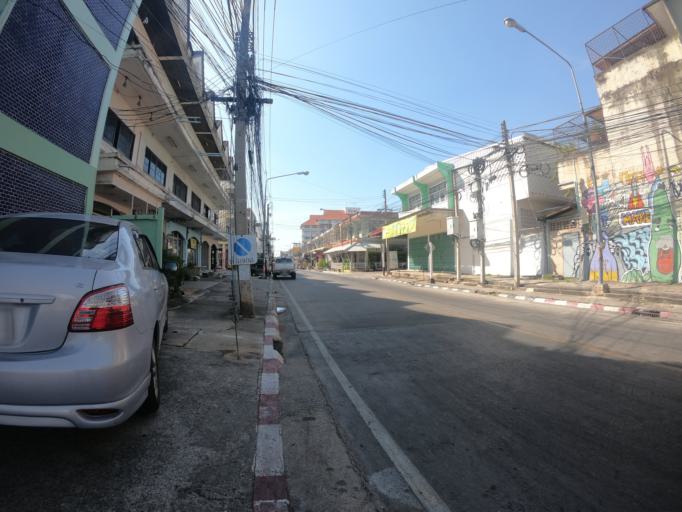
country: TH
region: Khon Kaen
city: Khon Kaen
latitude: 16.4367
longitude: 102.8344
